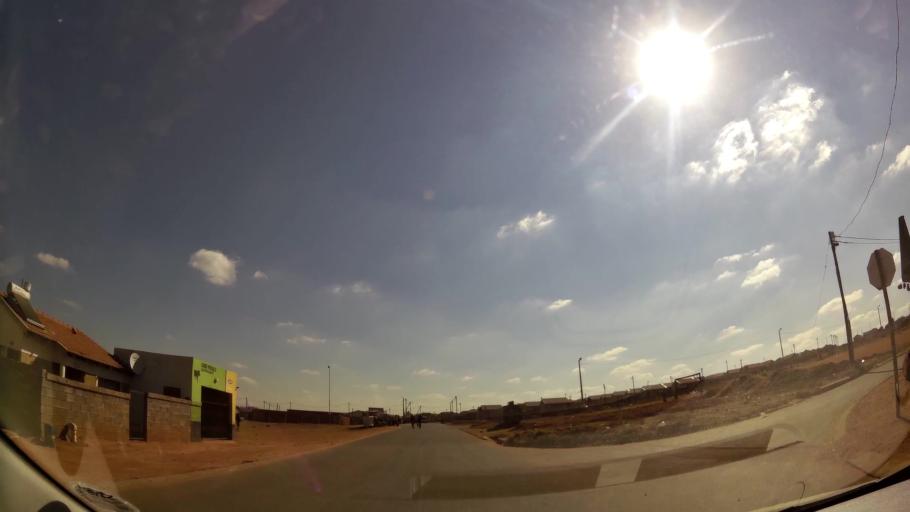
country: ZA
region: Gauteng
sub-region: West Rand District Municipality
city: Randfontein
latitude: -26.1699
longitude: 27.7758
